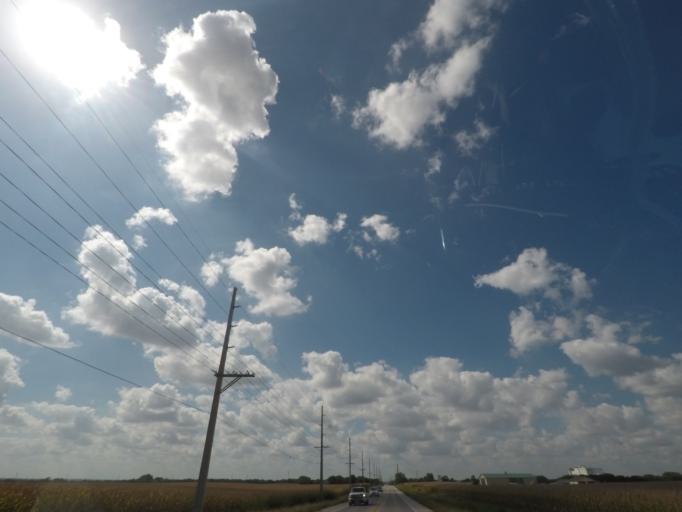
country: US
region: Iowa
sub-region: Story County
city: Ames
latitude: 42.0231
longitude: -93.5510
